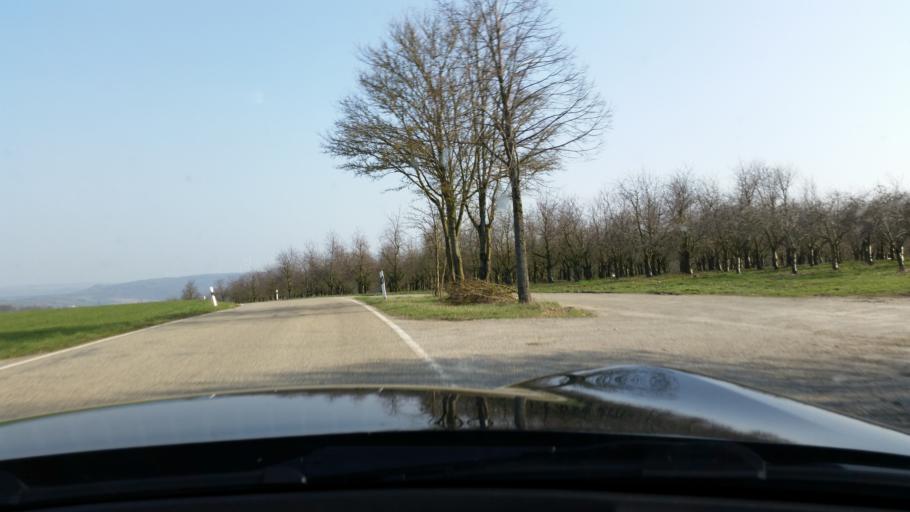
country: DE
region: Baden-Wuerttemberg
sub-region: Regierungsbezirk Stuttgart
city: Roigheim
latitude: 49.3385
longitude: 9.3243
